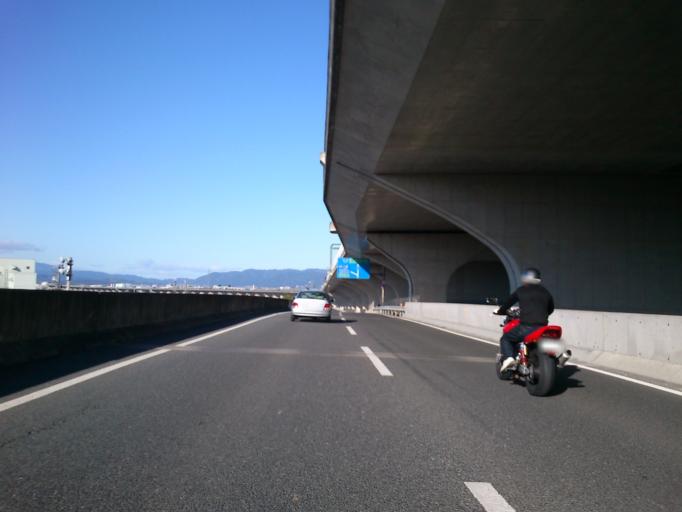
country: JP
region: Kyoto
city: Yawata
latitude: 34.8481
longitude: 135.7273
